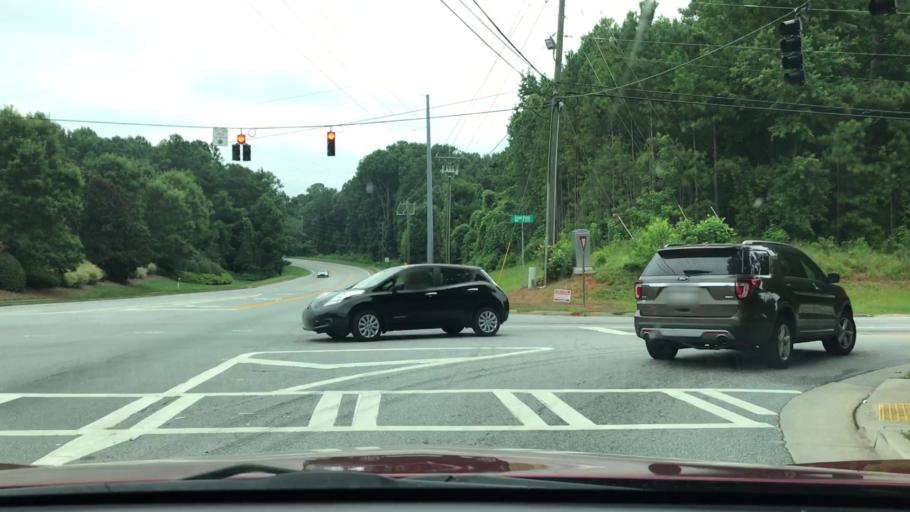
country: US
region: Georgia
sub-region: Gwinnett County
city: Suwanee
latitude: 34.0038
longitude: -84.0632
